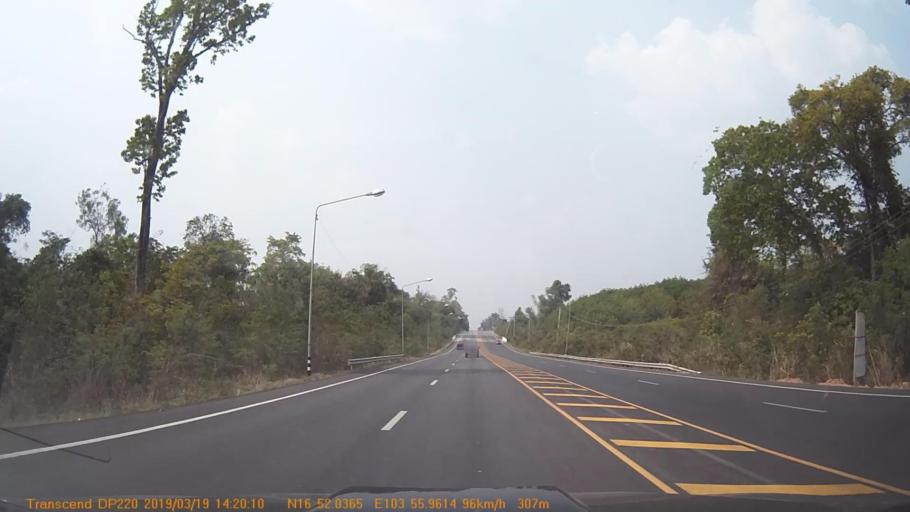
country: TH
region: Sakon Nakhon
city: Phu Phan
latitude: 16.8678
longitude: 103.9326
